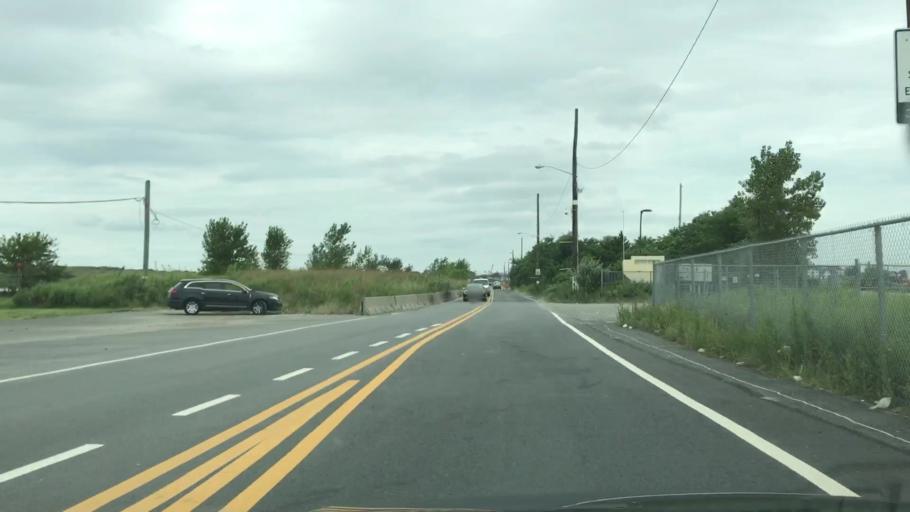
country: US
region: New Jersey
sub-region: Hudson County
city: Bayonne
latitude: 40.6680
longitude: -74.0890
